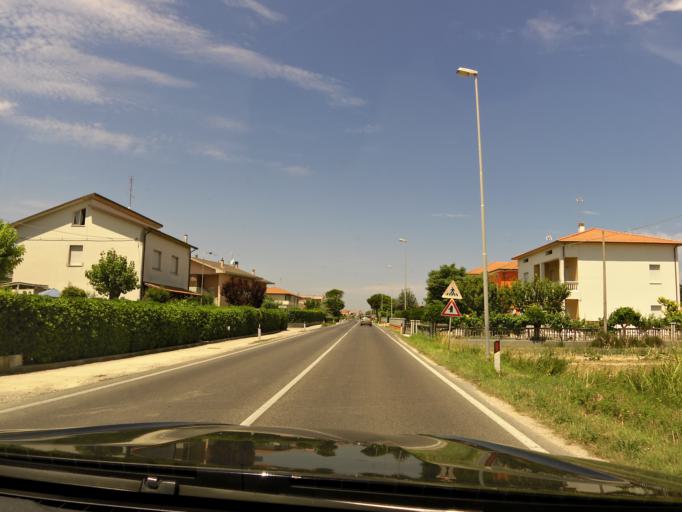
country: IT
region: The Marches
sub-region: Provincia di Pesaro e Urbino
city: Marotta
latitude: 43.7811
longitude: 13.1190
